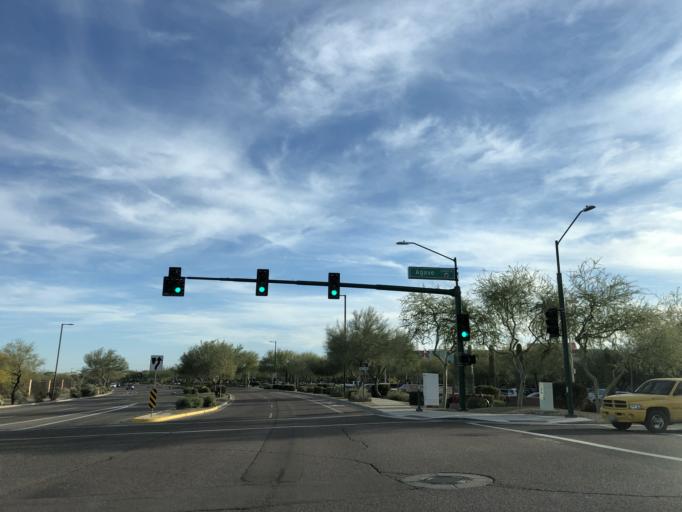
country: US
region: Arizona
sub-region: Maricopa County
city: Anthem
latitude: 33.7189
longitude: -112.1153
